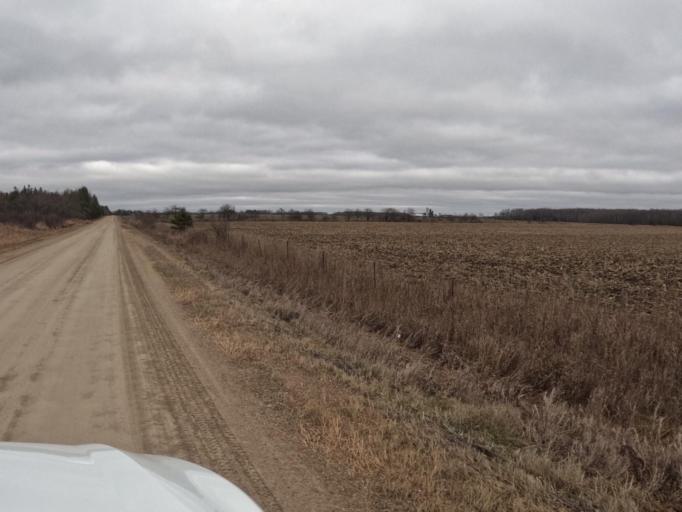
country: CA
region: Ontario
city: Shelburne
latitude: 43.9439
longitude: -80.3953
